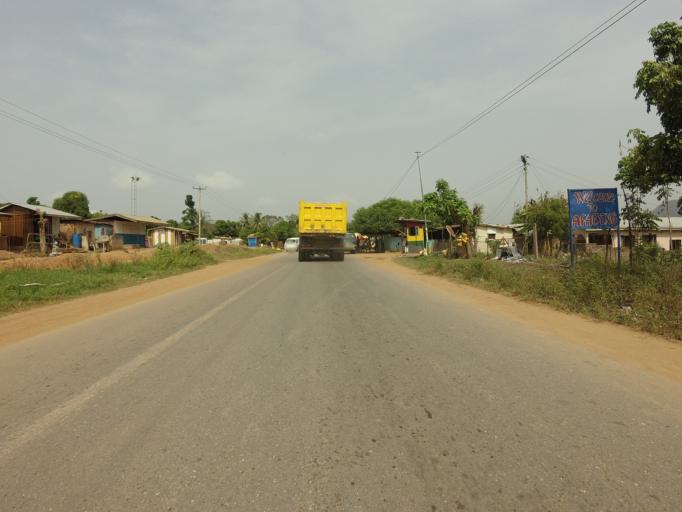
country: GH
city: Akropong
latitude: 6.2480
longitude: 0.0860
